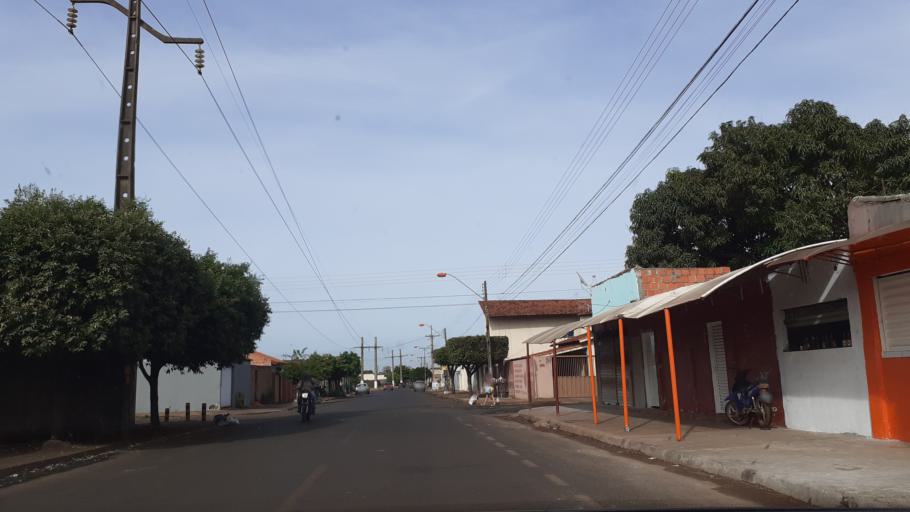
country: BR
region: Goias
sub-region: Itumbiara
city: Itumbiara
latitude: -18.4178
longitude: -49.2451
